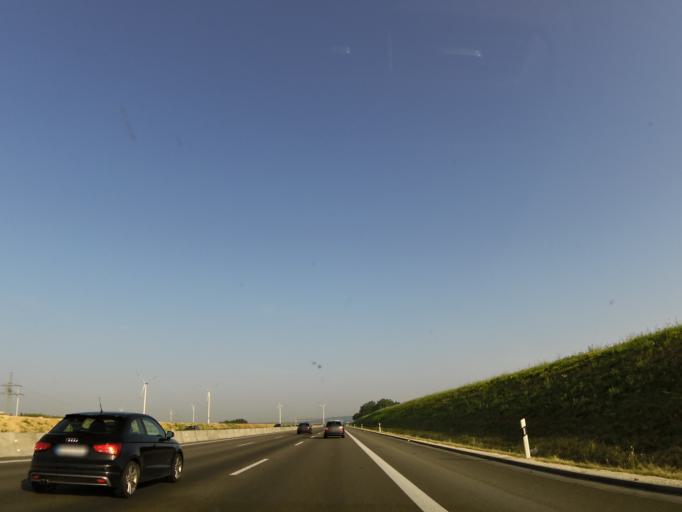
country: DE
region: Baden-Wuerttemberg
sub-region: Tuebingen Region
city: Dornstadt
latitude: 48.4702
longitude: 9.9032
